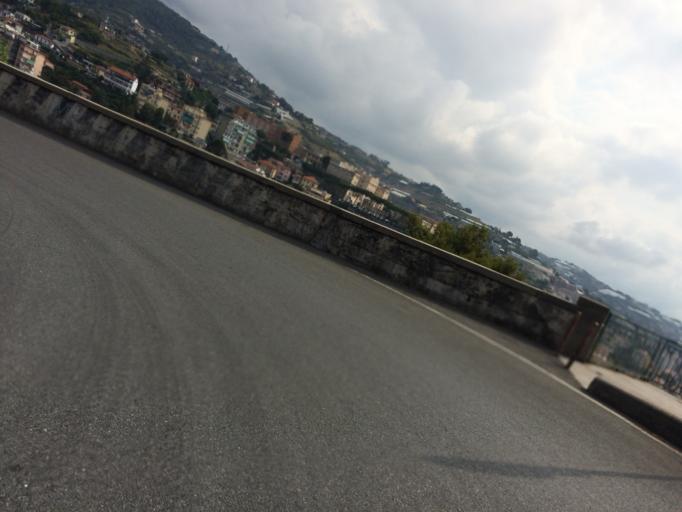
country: IT
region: Liguria
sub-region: Provincia di Imperia
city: San Remo
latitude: 43.8201
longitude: 7.7748
